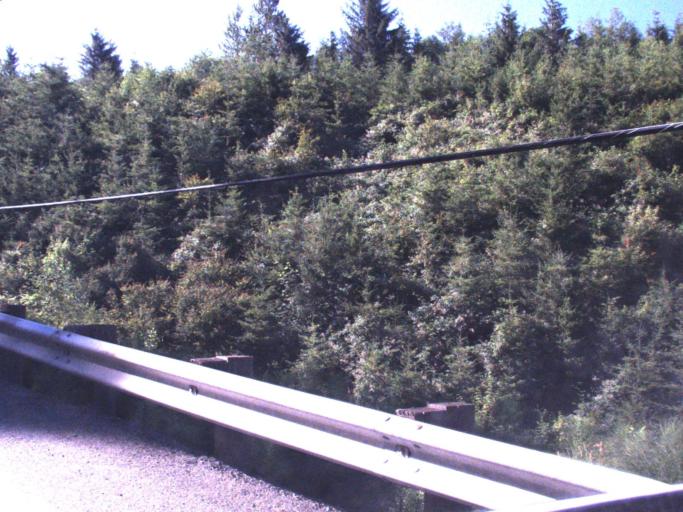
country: US
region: Washington
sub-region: King County
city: Enumclaw
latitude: 47.1653
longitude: -121.9101
